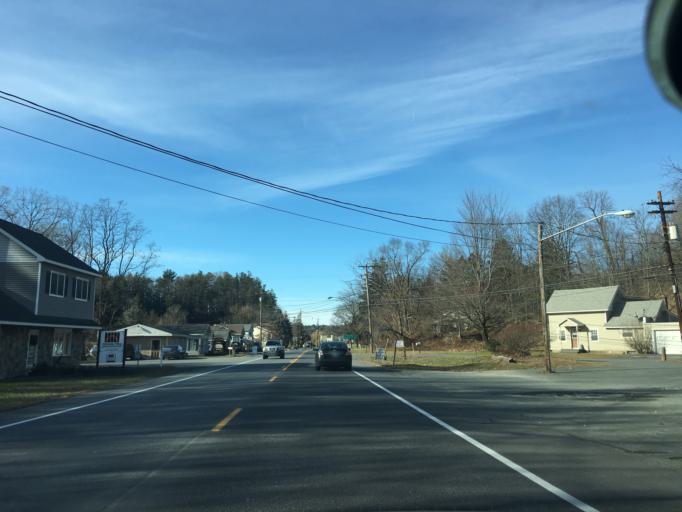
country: US
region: New York
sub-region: Rensselaer County
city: West Sand Lake
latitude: 42.6455
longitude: -73.5945
